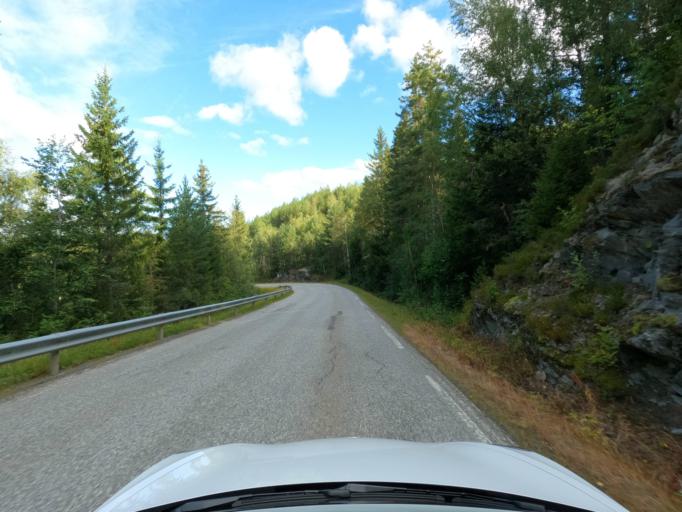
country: NO
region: Telemark
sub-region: Tinn
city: Rjukan
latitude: 59.9714
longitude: 8.8648
